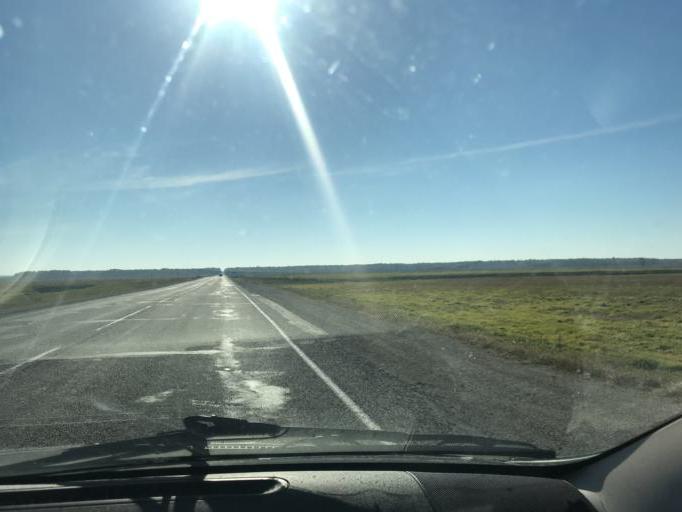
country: BY
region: Minsk
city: Starobin
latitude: 52.5256
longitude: 27.4740
